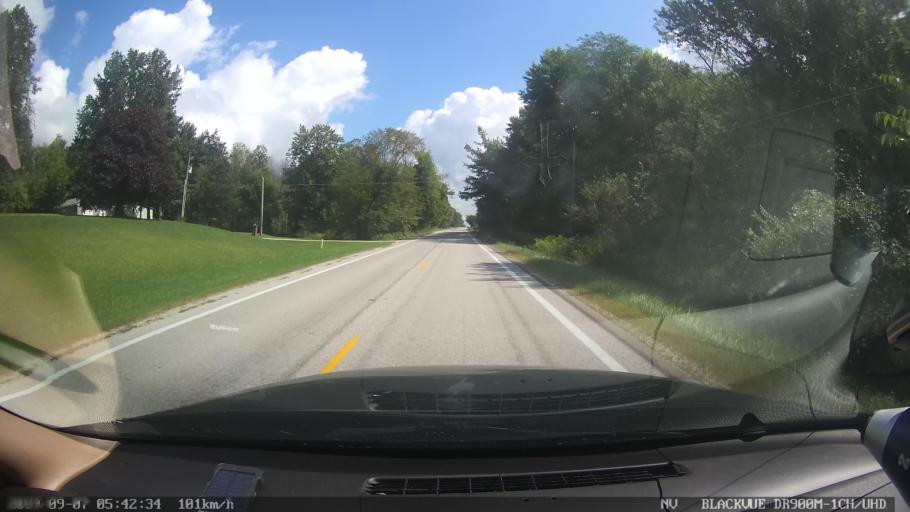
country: US
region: Ohio
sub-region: Crawford County
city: Galion
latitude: 40.6863
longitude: -82.7778
